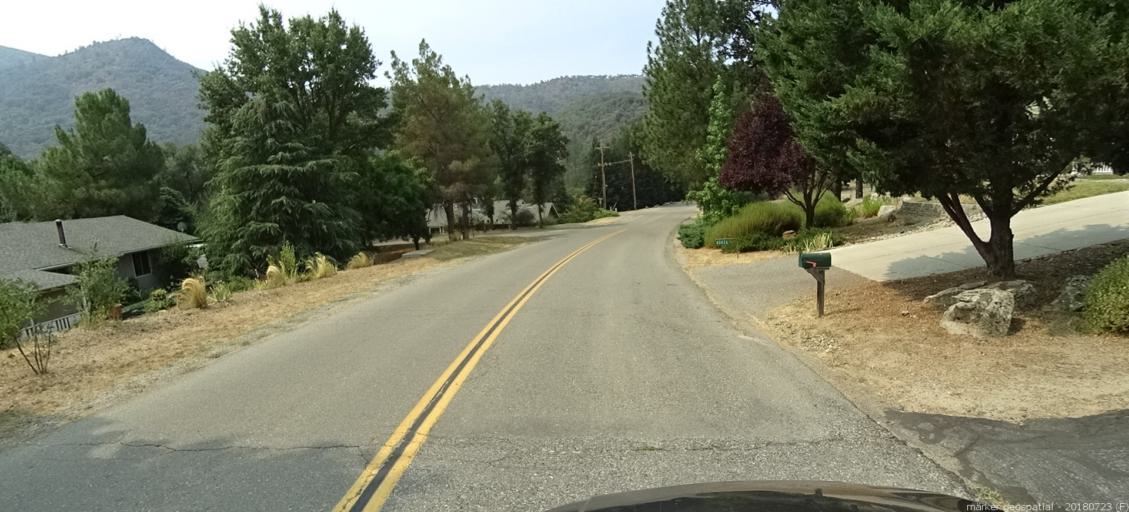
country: US
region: California
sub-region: Madera County
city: Ahwahnee
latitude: 37.3364
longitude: -119.7089
